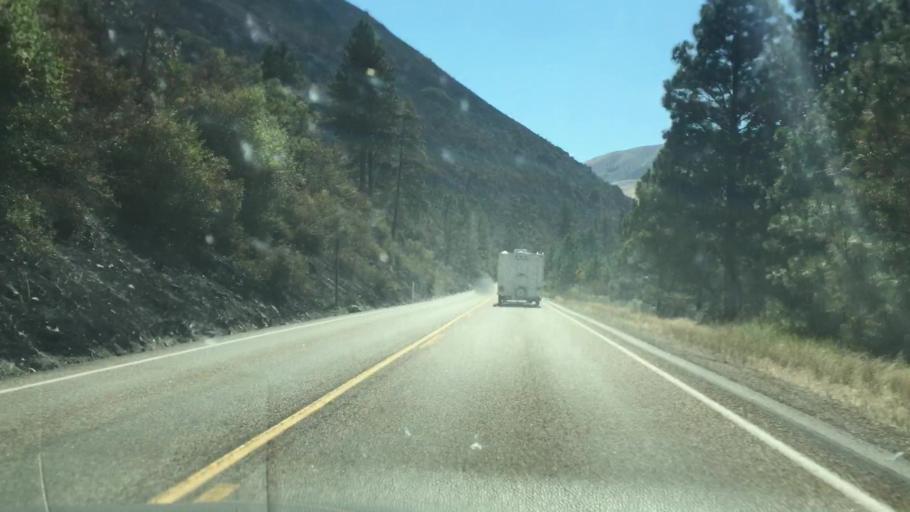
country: US
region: Idaho
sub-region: Gem County
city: Emmett
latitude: 44.0095
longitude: -116.1643
